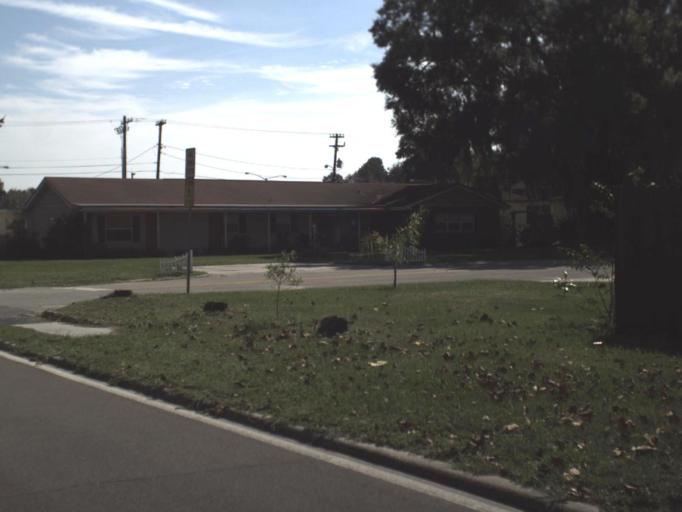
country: US
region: Florida
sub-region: Hardee County
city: Wauchula
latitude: 27.5489
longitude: -81.8027
